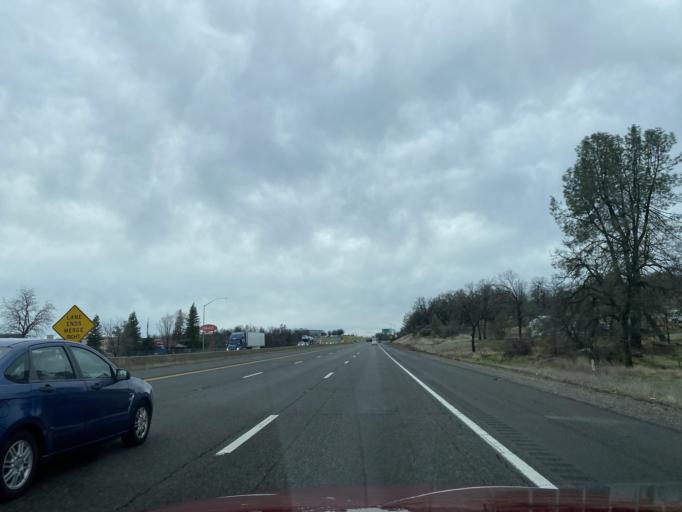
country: US
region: California
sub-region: Shasta County
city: Shasta Lake
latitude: 40.6358
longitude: -122.3673
